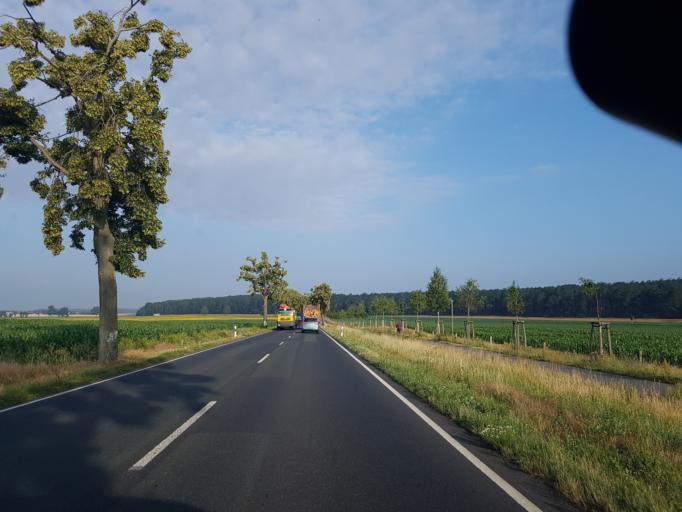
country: DE
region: Brandenburg
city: Schlieben
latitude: 51.7338
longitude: 13.3479
